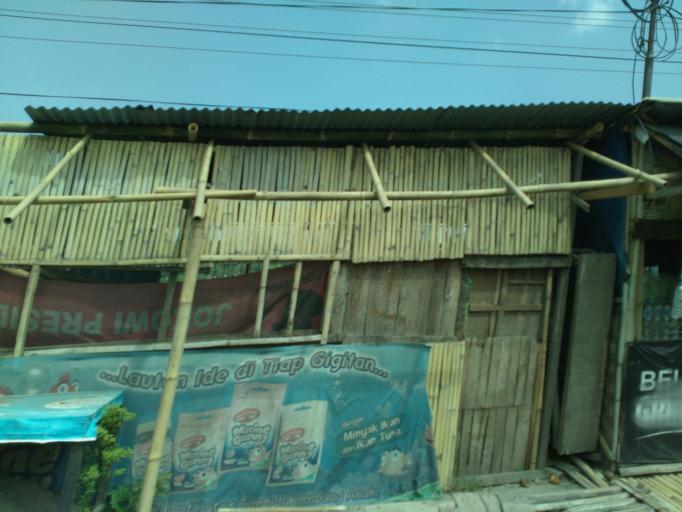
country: ID
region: Central Java
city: Candi Prambanan
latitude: -7.7487
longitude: 110.5224
